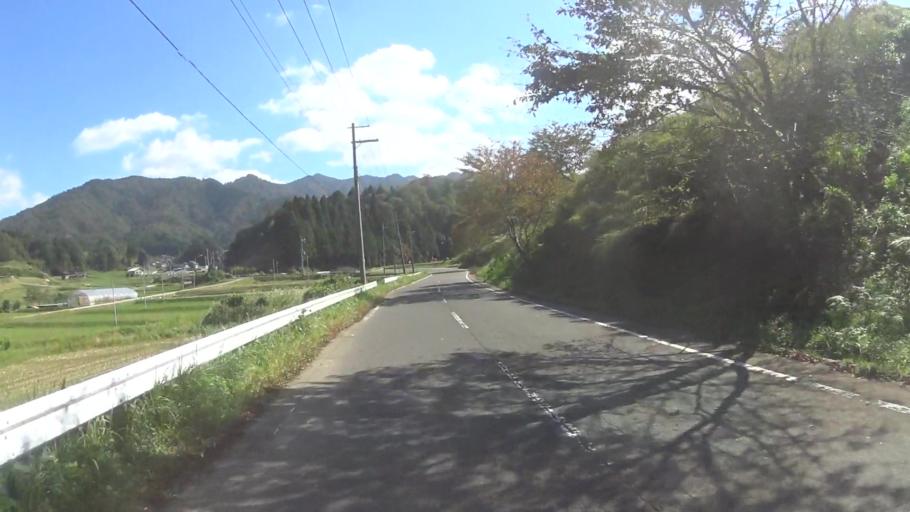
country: JP
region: Hyogo
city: Toyooka
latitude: 35.5436
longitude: 134.9413
